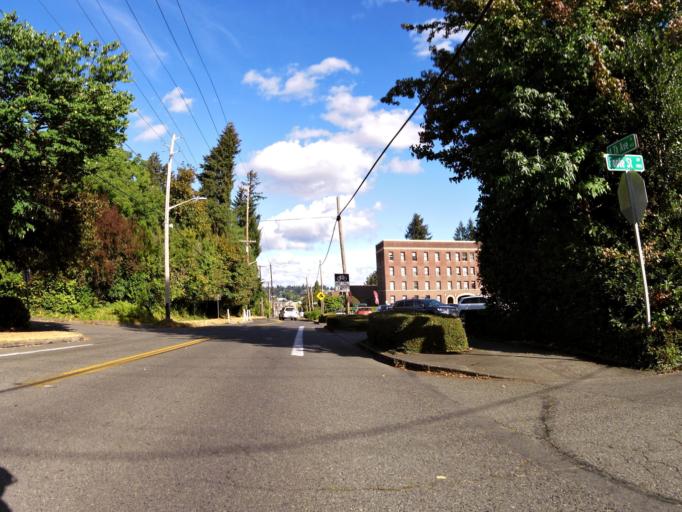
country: US
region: Washington
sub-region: Thurston County
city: Olympia
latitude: 47.0442
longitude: -122.9160
